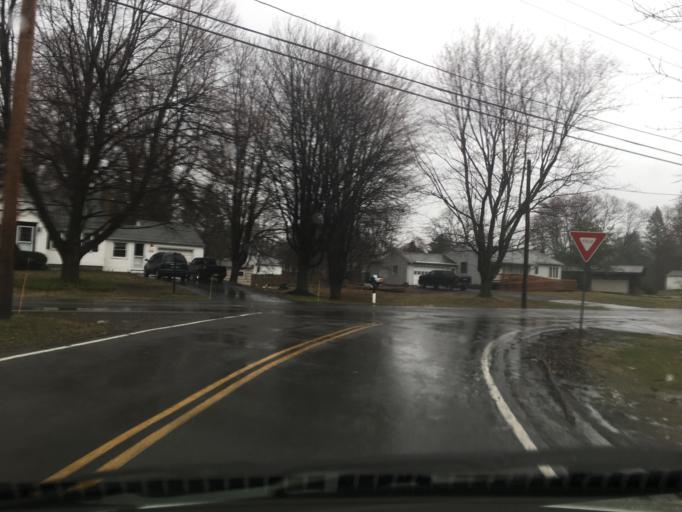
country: US
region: New York
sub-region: Monroe County
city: Brighton
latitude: 43.1725
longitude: -77.5035
